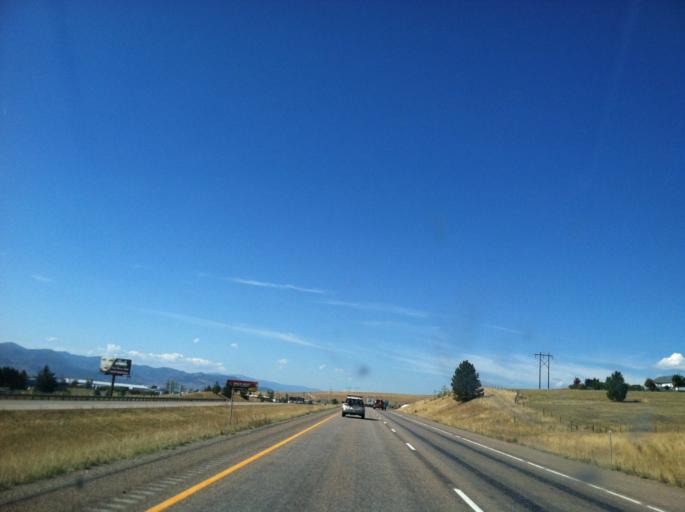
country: US
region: Montana
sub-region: Missoula County
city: Orchard Homes
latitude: 46.9332
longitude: -114.0878
